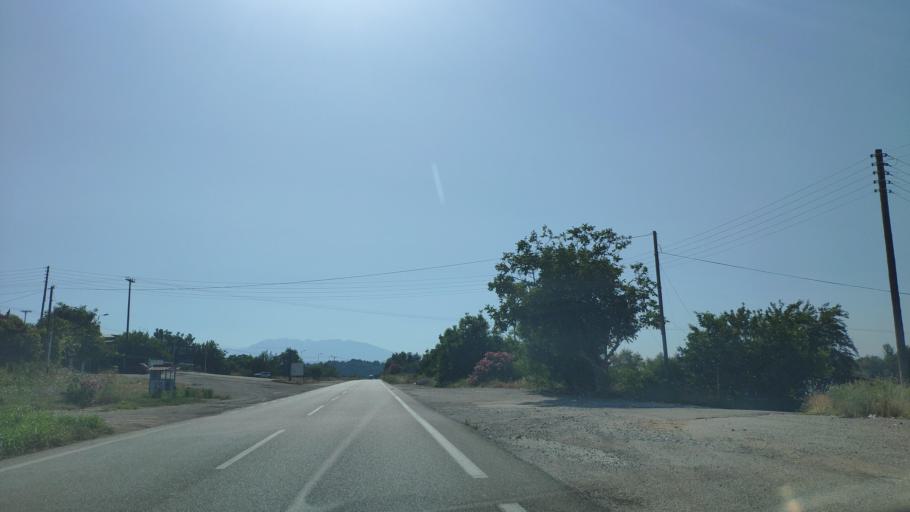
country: GR
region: West Greece
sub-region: Nomos Aitolias kai Akarnanias
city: Lepenou
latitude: 38.6868
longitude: 21.2418
